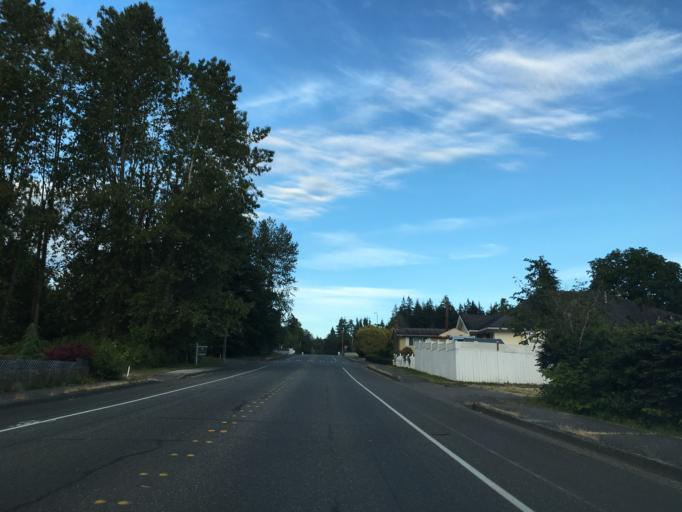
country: US
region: Washington
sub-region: Whatcom County
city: Blaine
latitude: 48.9981
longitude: -122.7377
